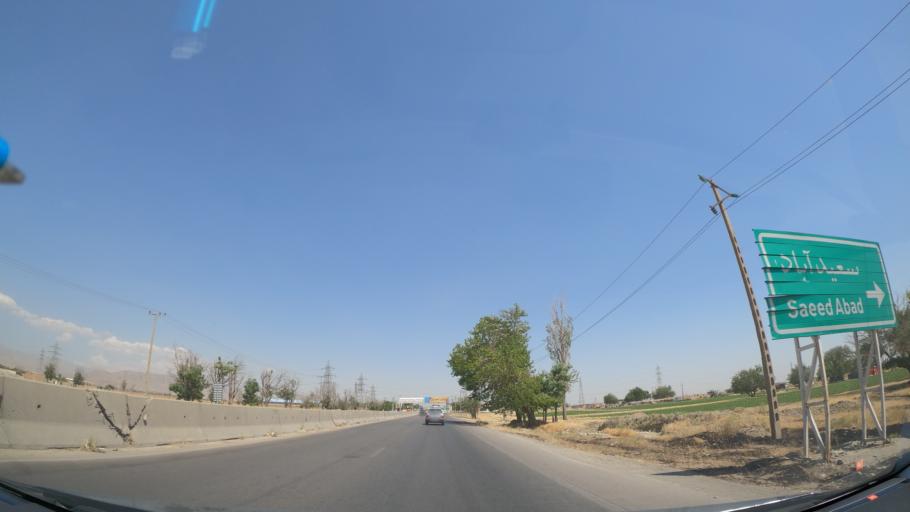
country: IR
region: Alborz
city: Hashtgerd
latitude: 35.9248
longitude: 50.7391
